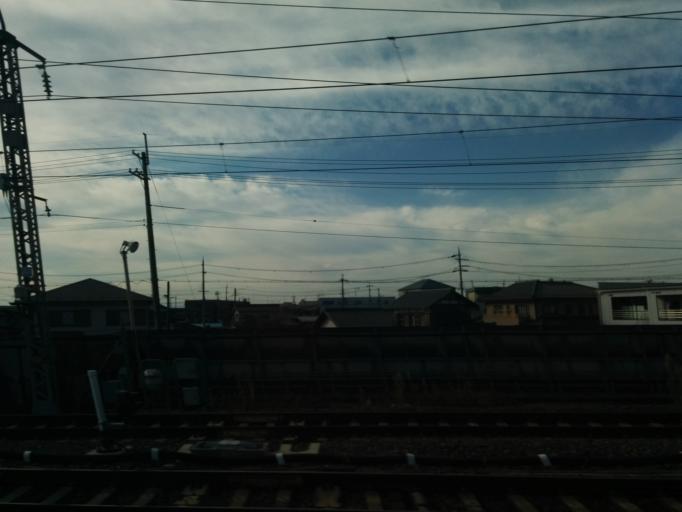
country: JP
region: Shiga Prefecture
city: Hikone
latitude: 35.3124
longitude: 136.2885
